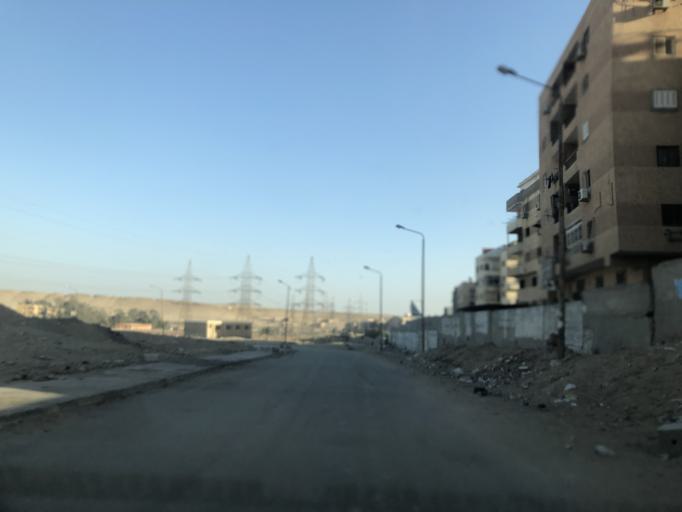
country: EG
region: Al Jizah
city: Al Jizah
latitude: 29.9849
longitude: 31.1086
